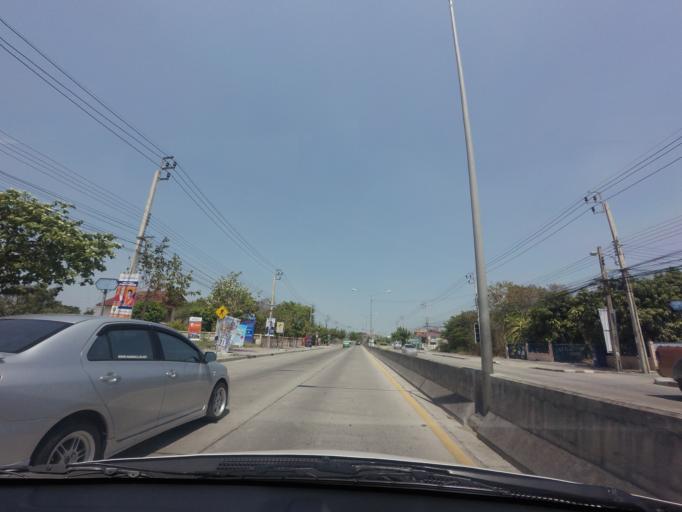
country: TH
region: Bangkok
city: Khlong Sam Wa
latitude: 13.8342
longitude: 100.7753
